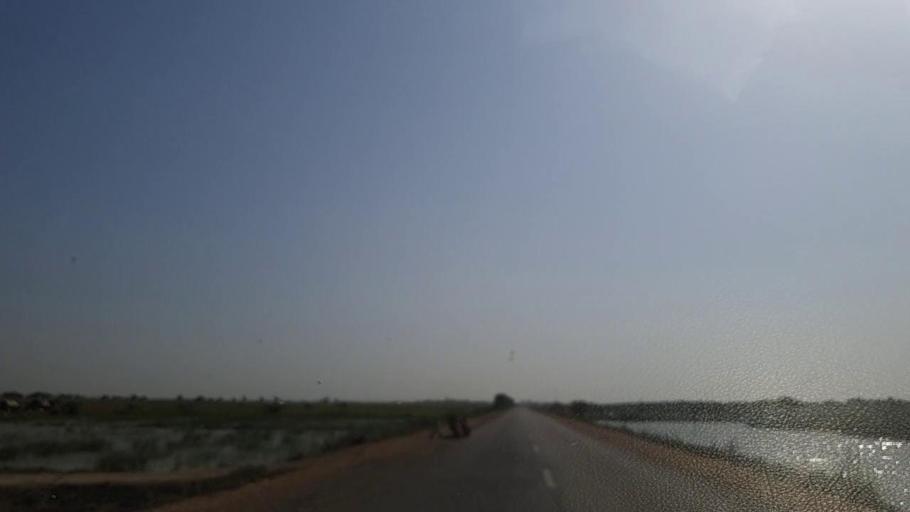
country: PK
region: Sindh
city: Jati
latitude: 24.5376
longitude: 68.2792
